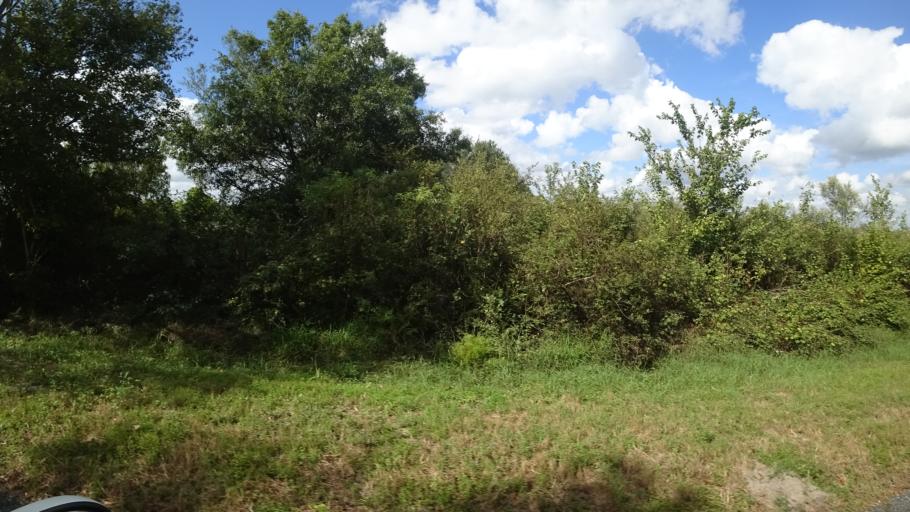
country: US
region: Florida
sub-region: Hillsborough County
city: Wimauma
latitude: 27.4758
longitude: -82.1706
